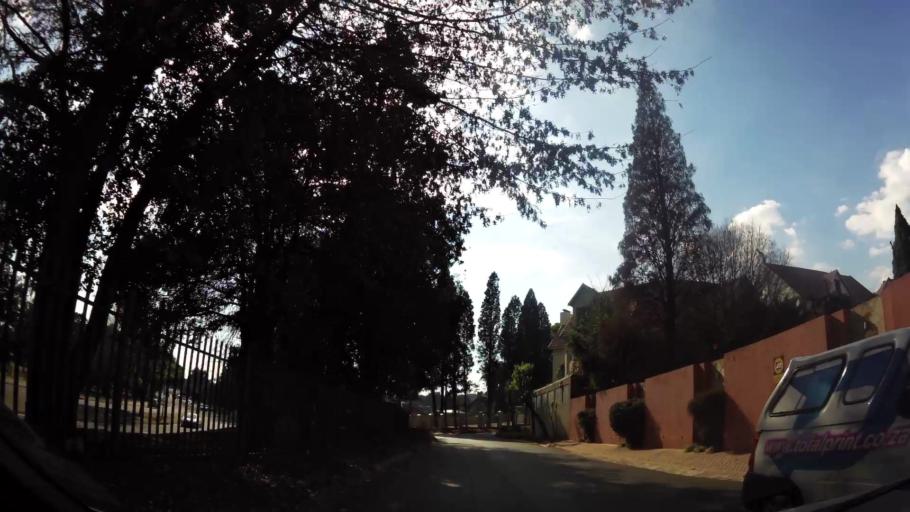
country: ZA
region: Gauteng
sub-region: Ekurhuleni Metropolitan Municipality
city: Germiston
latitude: -26.1913
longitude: 28.1351
